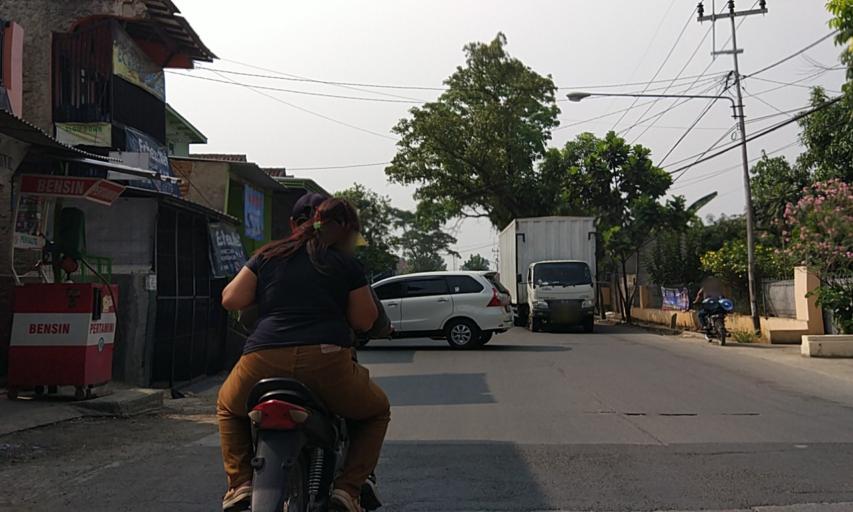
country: ID
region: West Java
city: Soreang
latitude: -7.0268
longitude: 107.5482
